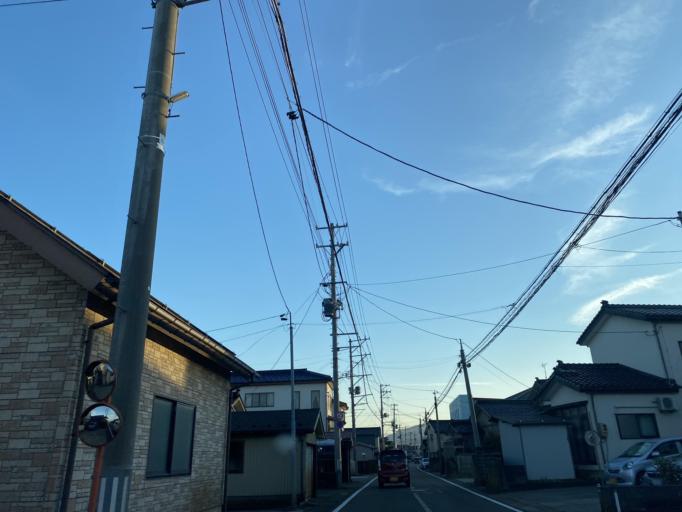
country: JP
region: Niigata
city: Kashiwazaki
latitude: 37.3834
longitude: 138.5688
